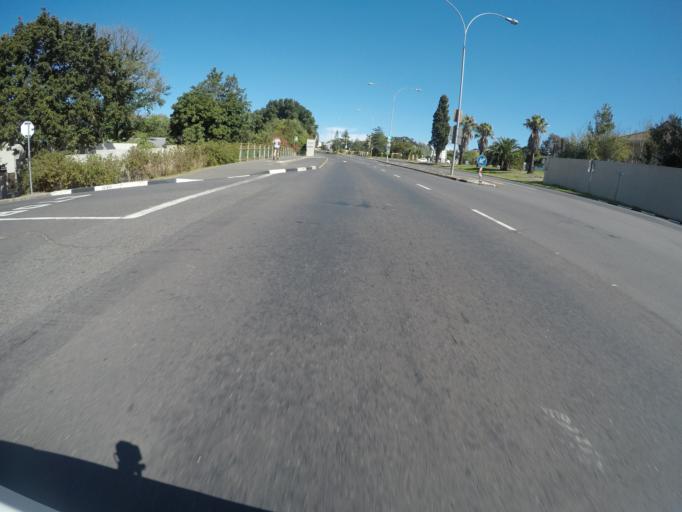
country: ZA
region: Western Cape
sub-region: City of Cape Town
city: Kraaifontein
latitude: -33.8445
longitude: 18.6456
